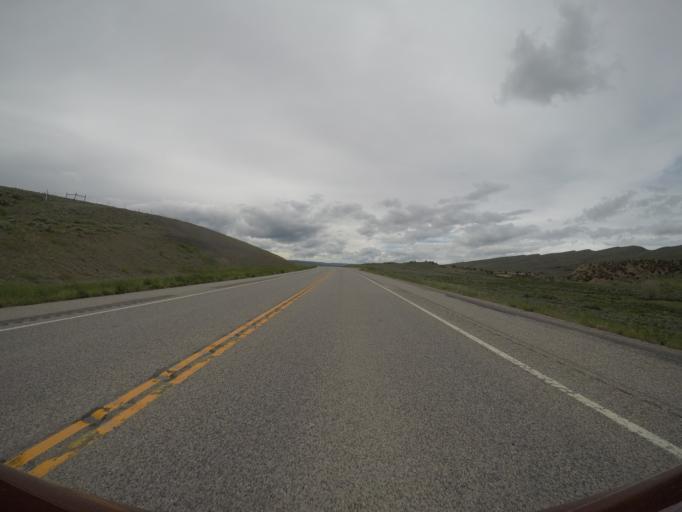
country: US
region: Wyoming
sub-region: Park County
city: Powell
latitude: 45.1385
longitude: -108.7819
